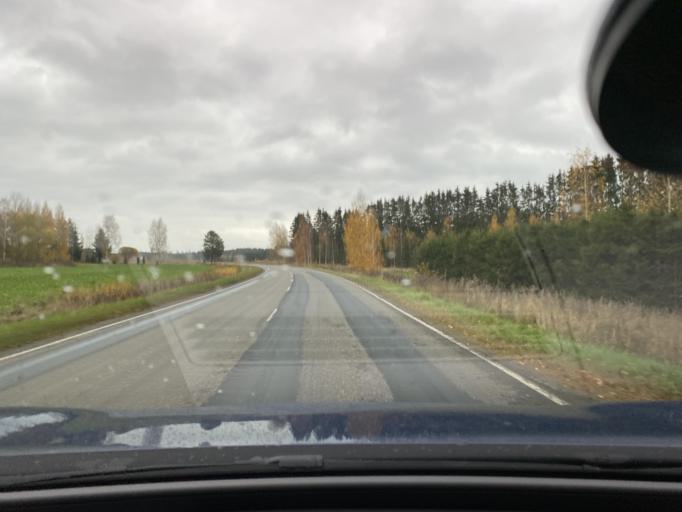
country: FI
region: Satakunta
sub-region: Rauma
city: Saekylae
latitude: 61.0400
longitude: 22.4001
